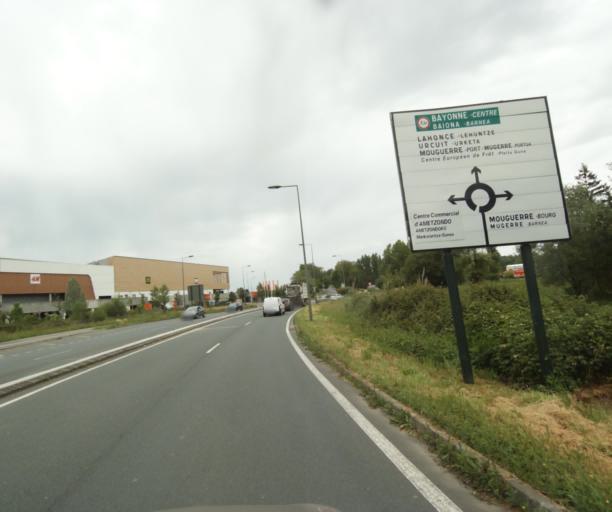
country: FR
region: Aquitaine
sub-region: Departement des Pyrenees-Atlantiques
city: Mouguerre
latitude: 43.4809
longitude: -1.4427
